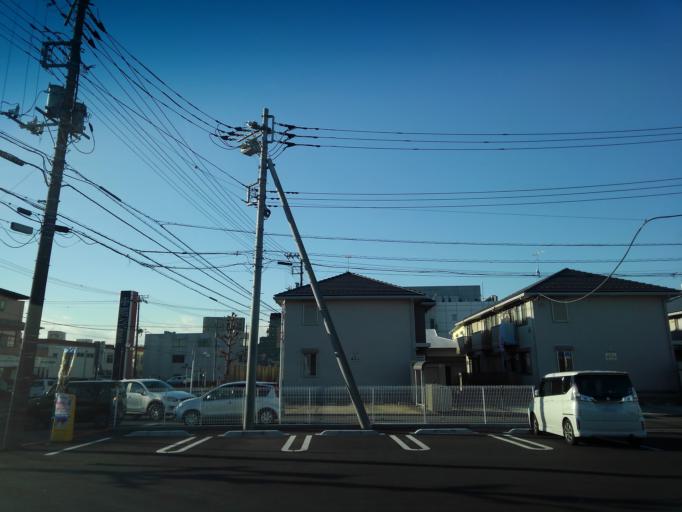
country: JP
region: Chiba
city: Kimitsu
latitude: 35.3349
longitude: 139.8973
